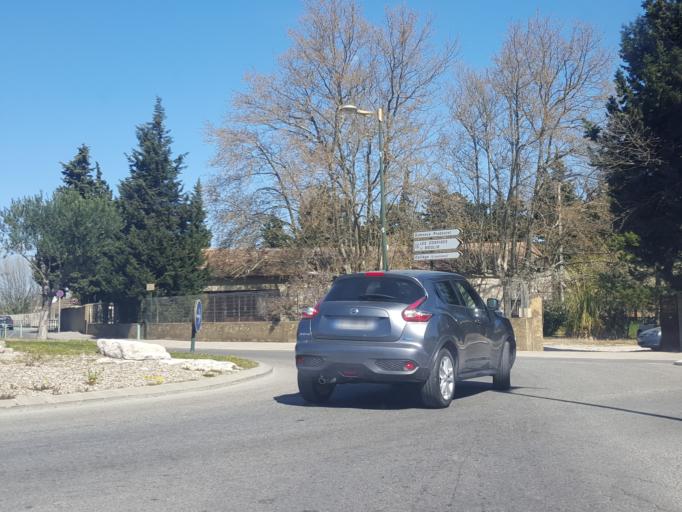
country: FR
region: Provence-Alpes-Cote d'Azur
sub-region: Departement du Vaucluse
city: Vedene
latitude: 43.9772
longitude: 4.9091
